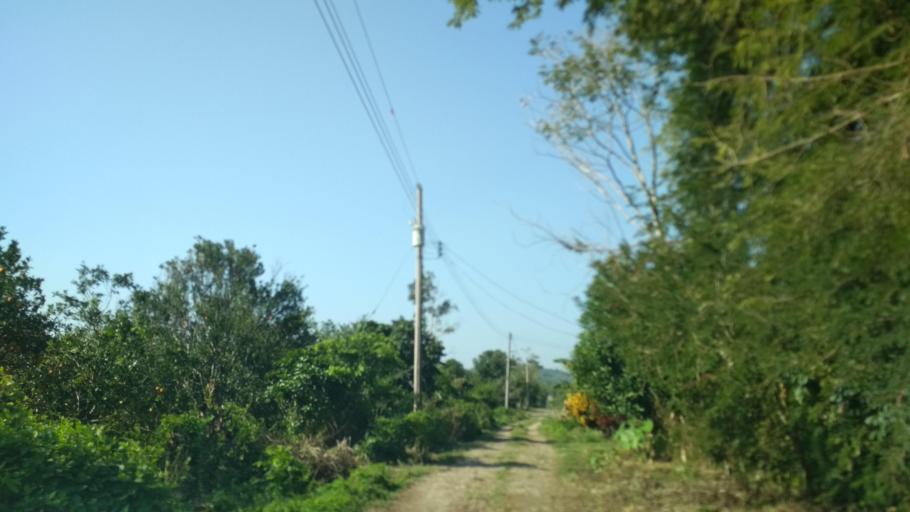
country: MX
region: Veracruz
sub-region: Papantla
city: Polutla
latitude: 20.4505
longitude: -97.2140
